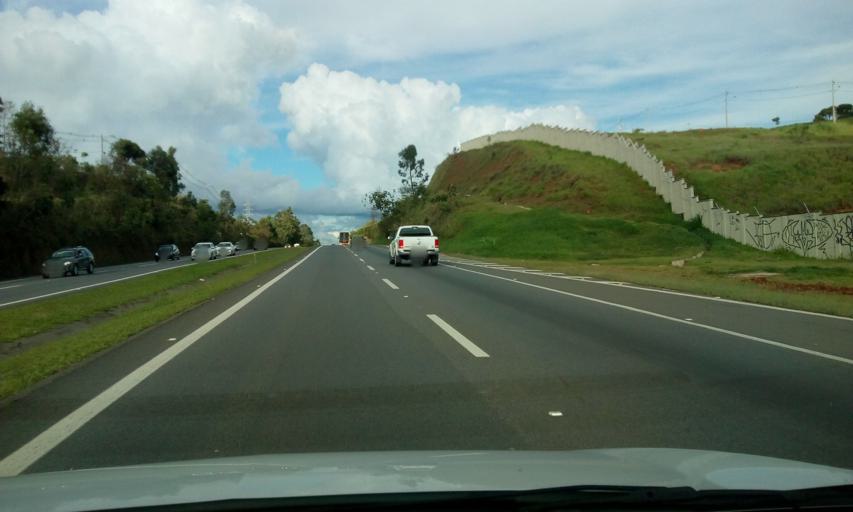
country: BR
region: Sao Paulo
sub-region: Jundiai
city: Jundiai
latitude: -23.1584
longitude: -46.8963
